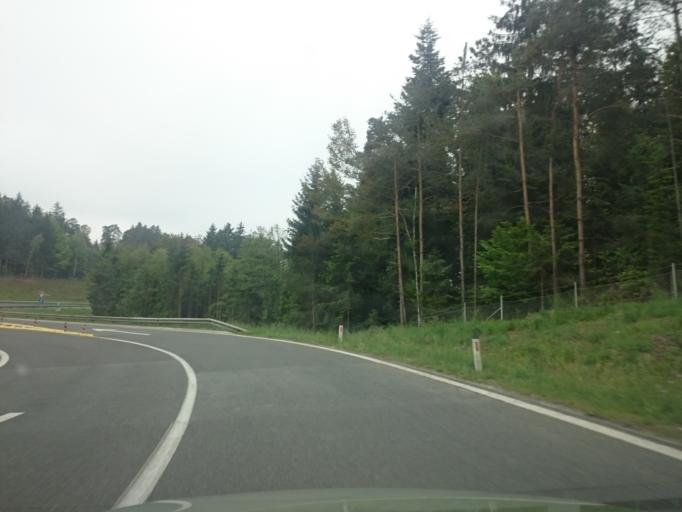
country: SI
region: Sentjur pri Celju
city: Sentjur
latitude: 46.2643
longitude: 15.3908
